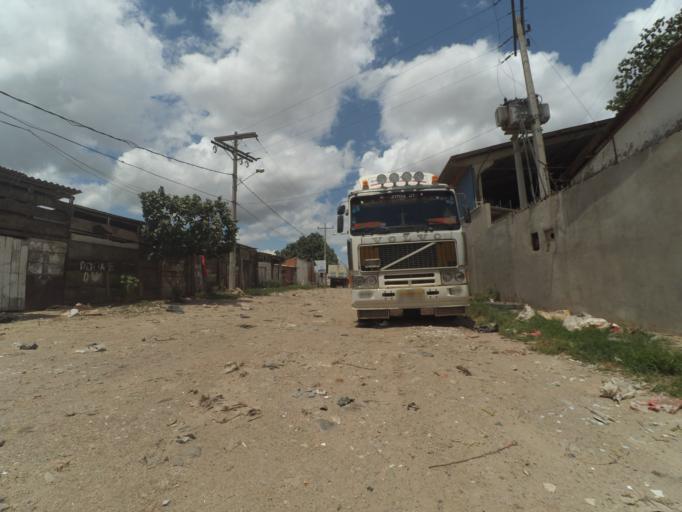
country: BO
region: Santa Cruz
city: Santa Cruz de la Sierra
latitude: -17.8142
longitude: -63.2144
